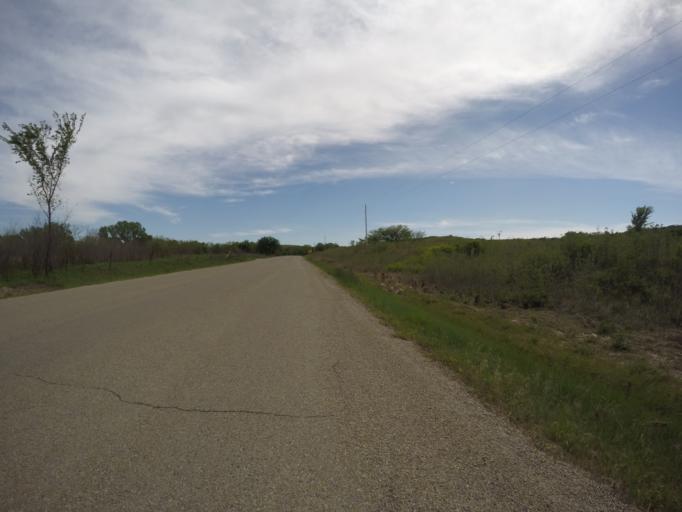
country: US
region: Kansas
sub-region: Riley County
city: Ogden
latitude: 39.0618
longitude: -96.6514
